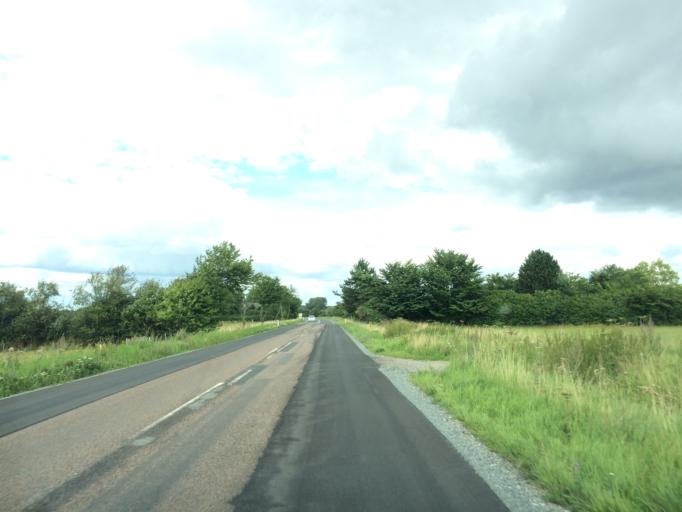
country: DK
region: South Denmark
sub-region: Assens Kommune
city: Tommerup
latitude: 55.2623
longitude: 10.2554
